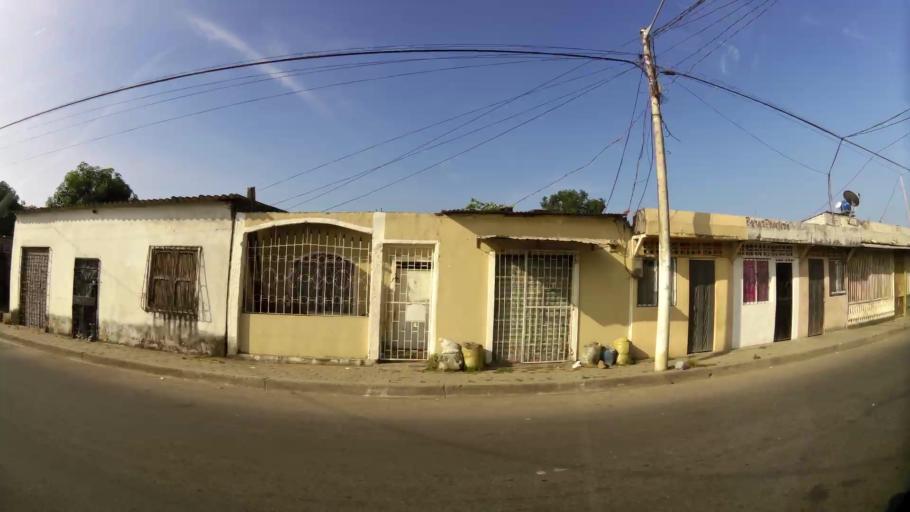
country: EC
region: Guayas
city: Eloy Alfaro
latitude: -2.1861
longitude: -79.8428
